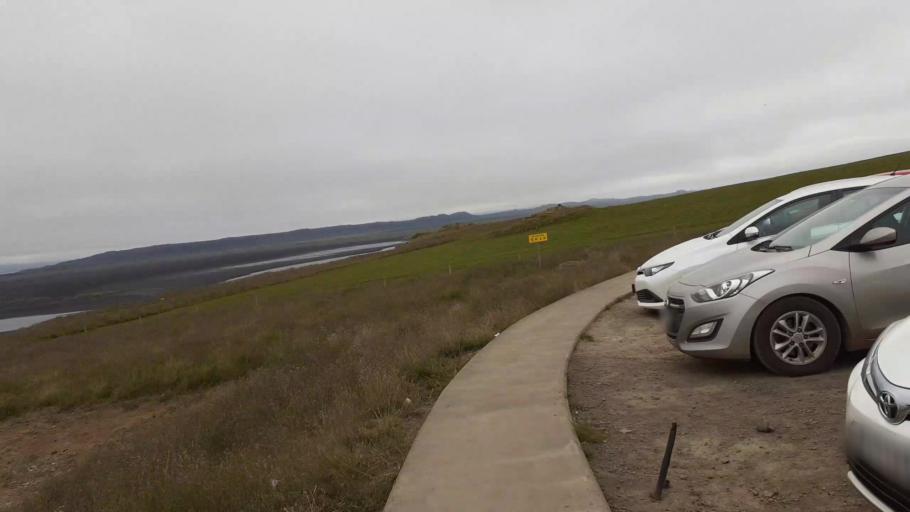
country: IS
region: Northwest
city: Saudarkrokur
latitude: 65.6038
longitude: -20.6395
